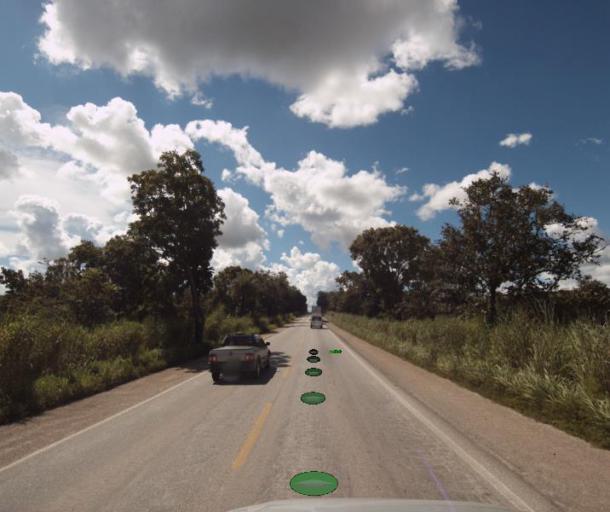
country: BR
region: Goias
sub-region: Porangatu
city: Porangatu
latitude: -13.6433
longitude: -49.0401
